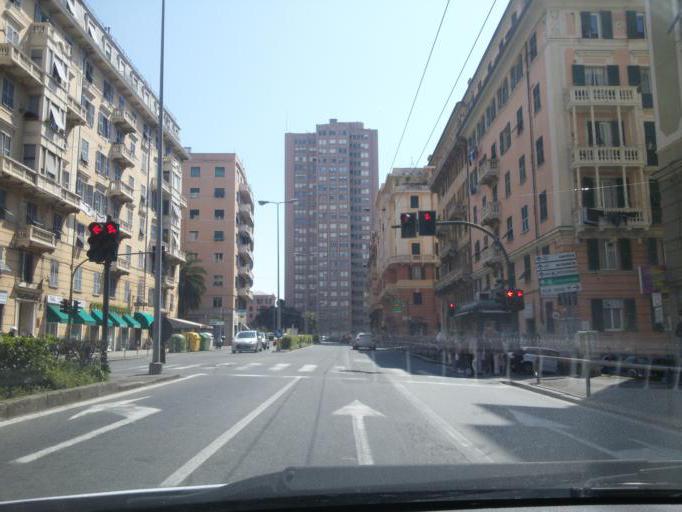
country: IT
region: Liguria
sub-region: Provincia di Genova
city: San Teodoro
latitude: 44.4108
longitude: 8.8971
